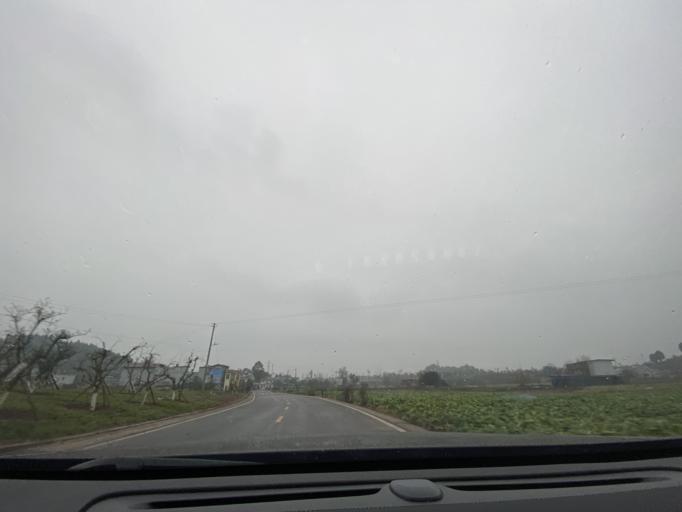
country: CN
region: Sichuan
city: Jiancheng
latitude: 30.3920
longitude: 104.6358
